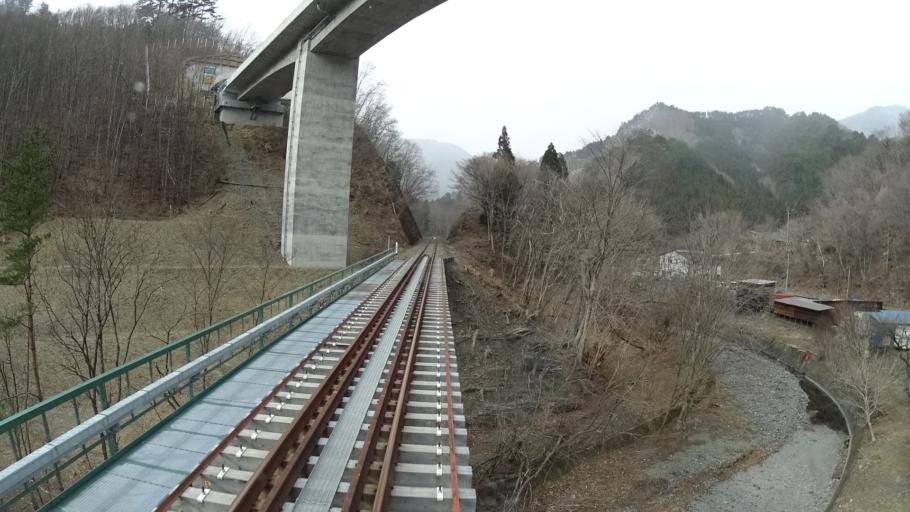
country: JP
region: Iwate
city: Kamaishi
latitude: 39.2957
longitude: 141.8660
